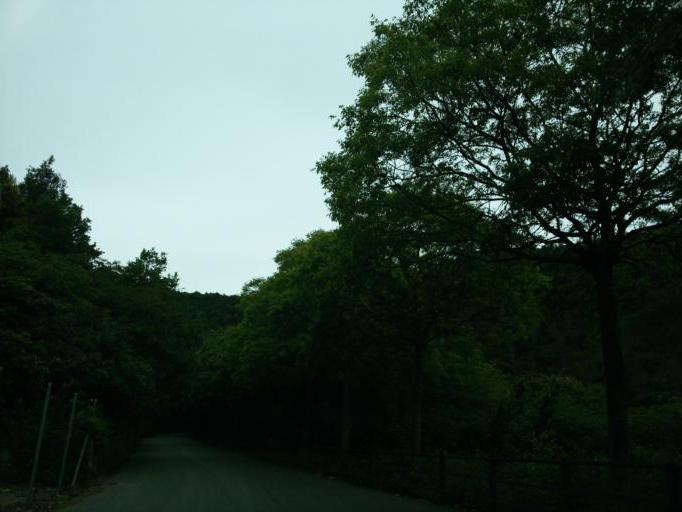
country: IT
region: Liguria
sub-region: Provincia di Genova
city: Genoa
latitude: 44.4322
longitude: 8.9266
